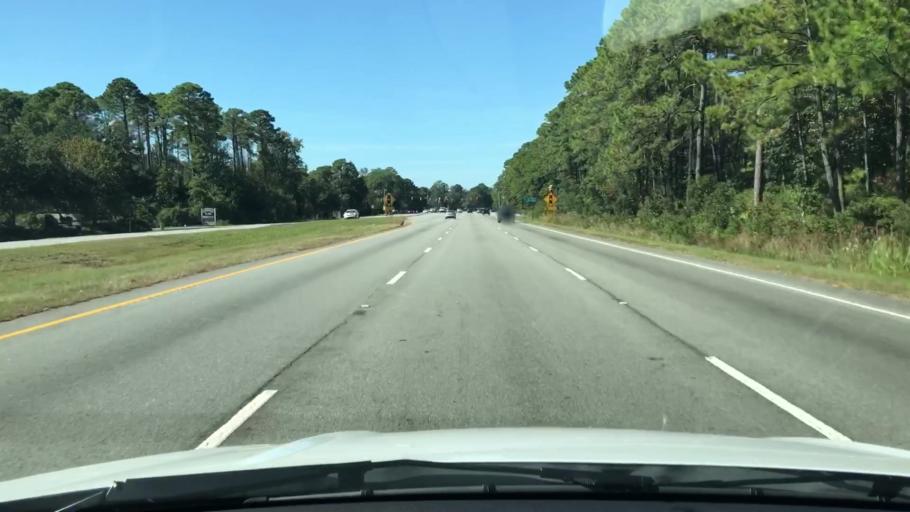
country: US
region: South Carolina
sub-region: Beaufort County
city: Bluffton
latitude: 32.2504
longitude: -80.8393
